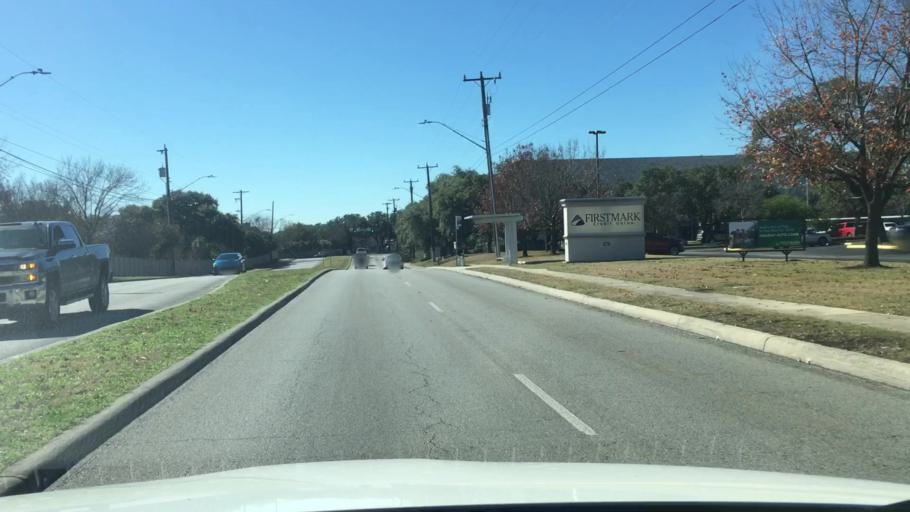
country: US
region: Texas
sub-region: Bexar County
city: Hollywood Park
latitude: 29.6041
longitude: -98.4585
